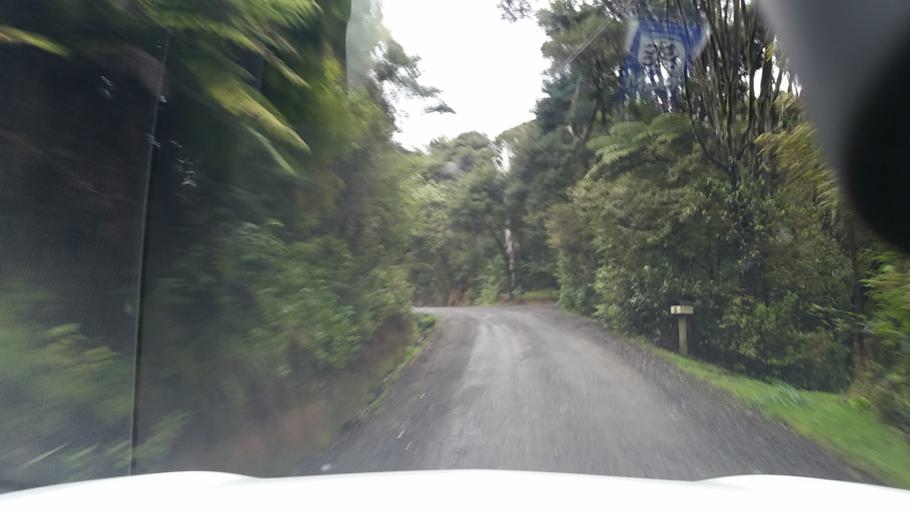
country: NZ
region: Auckland
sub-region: Auckland
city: Waitakere
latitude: -36.9013
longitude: 174.5711
